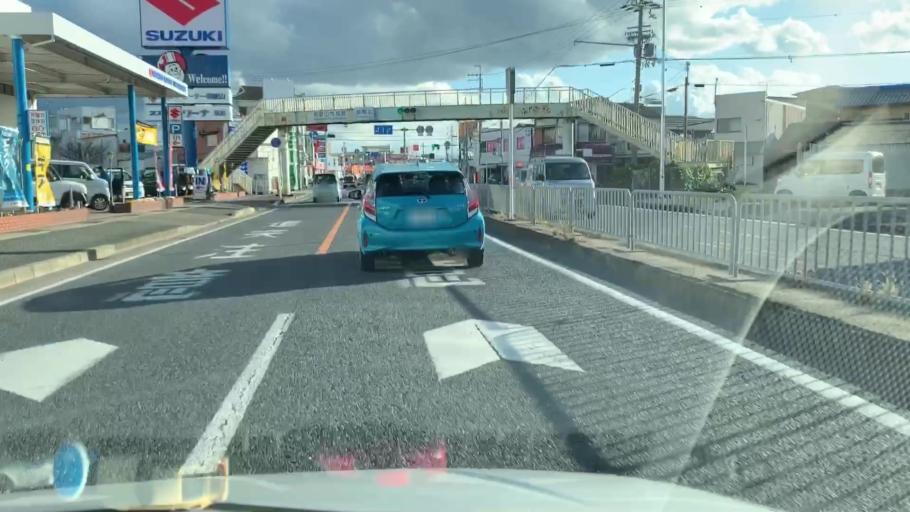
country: JP
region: Wakayama
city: Wakayama-shi
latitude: 34.2444
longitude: 135.1512
